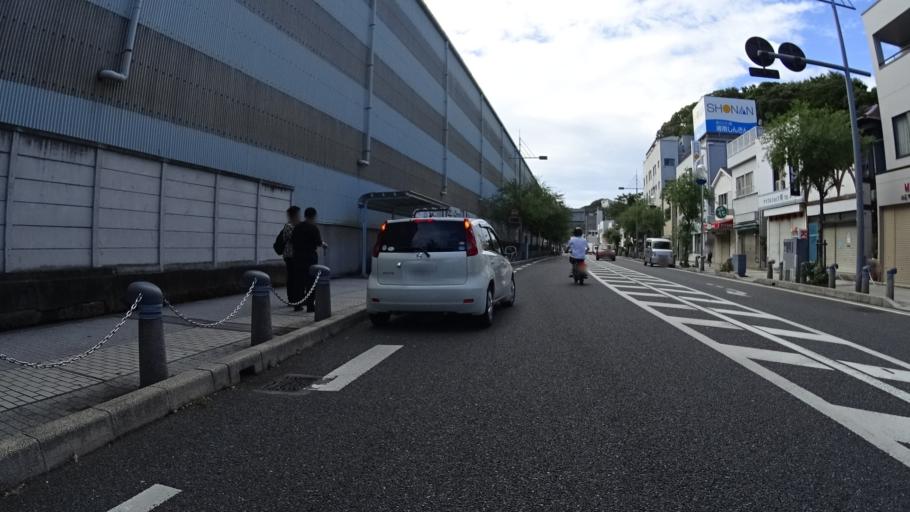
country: JP
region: Kanagawa
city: Yokosuka
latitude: 35.2496
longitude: 139.7150
